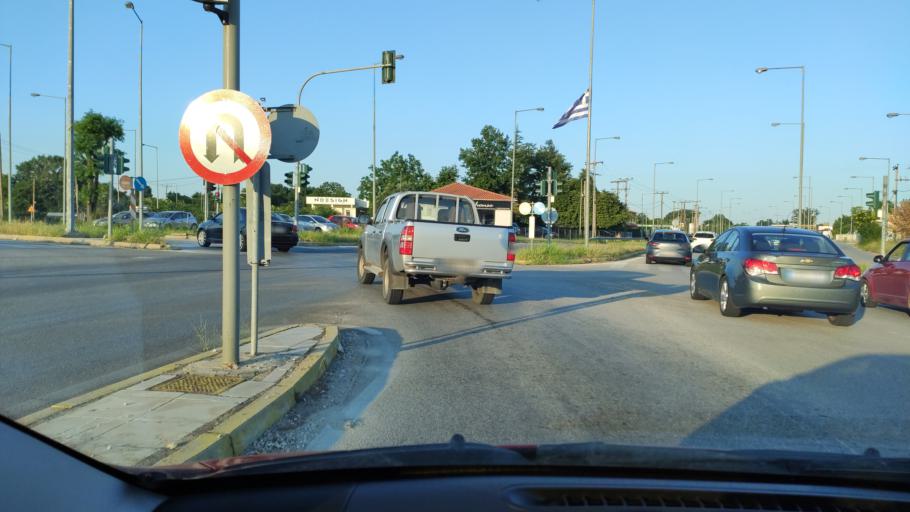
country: GR
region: East Macedonia and Thrace
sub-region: Nomos Rodopis
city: Komotini
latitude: 41.1143
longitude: 25.3800
